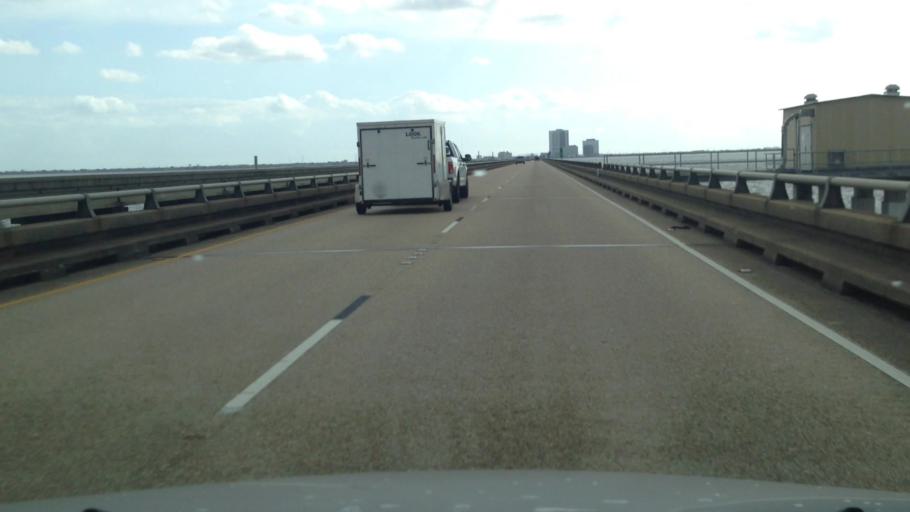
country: US
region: Louisiana
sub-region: Jefferson Parish
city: Metairie
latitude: 30.0547
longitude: -90.1485
